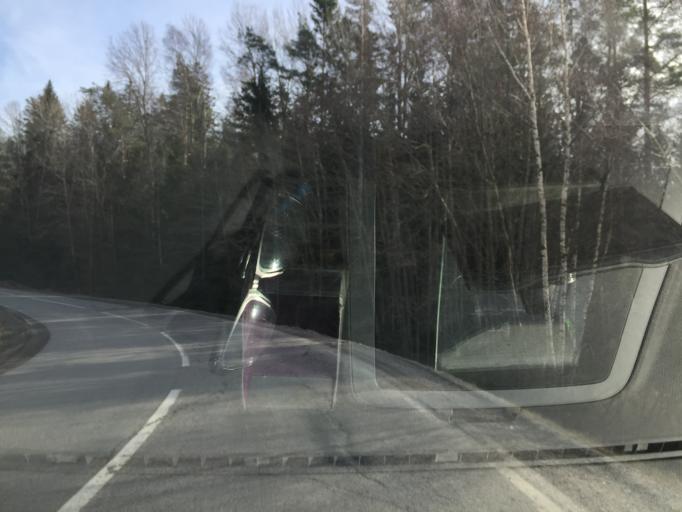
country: SE
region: Stockholm
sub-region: Haninge Kommun
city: Jordbro
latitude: 59.1243
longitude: 18.0080
